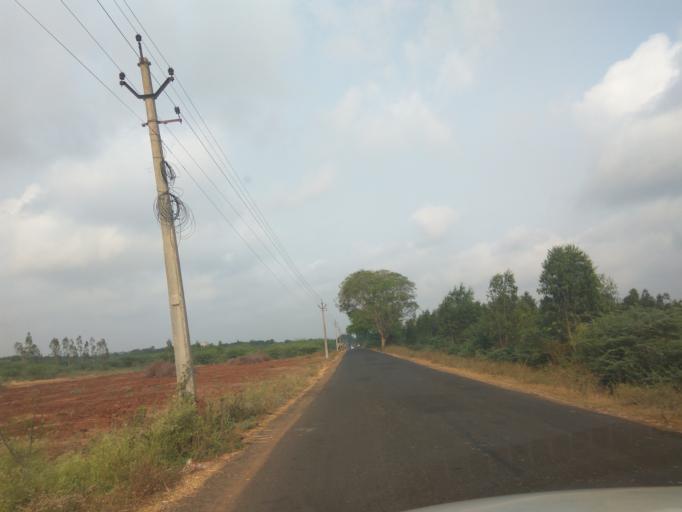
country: IN
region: Andhra Pradesh
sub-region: Prakasam
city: Kandukur
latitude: 15.2094
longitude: 79.8805
